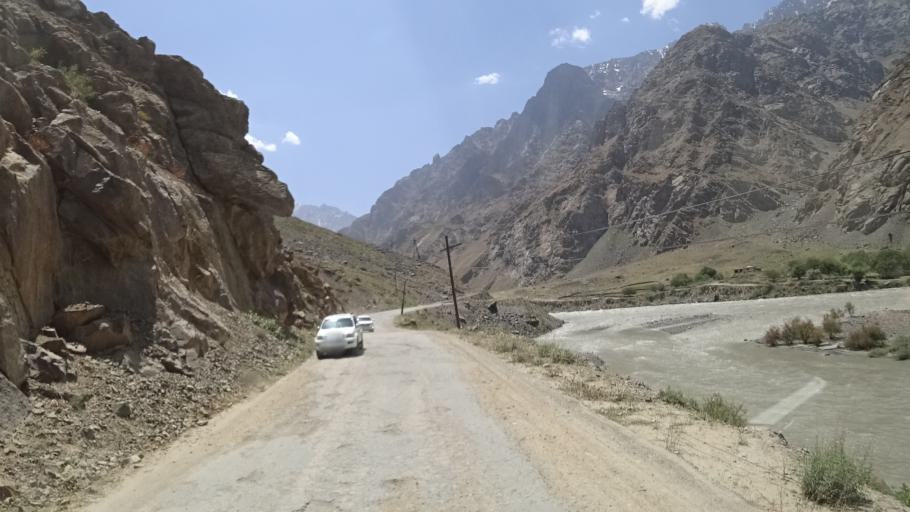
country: TJ
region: Gorno-Badakhshan
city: Rushon
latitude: 37.8472
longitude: 71.5869
